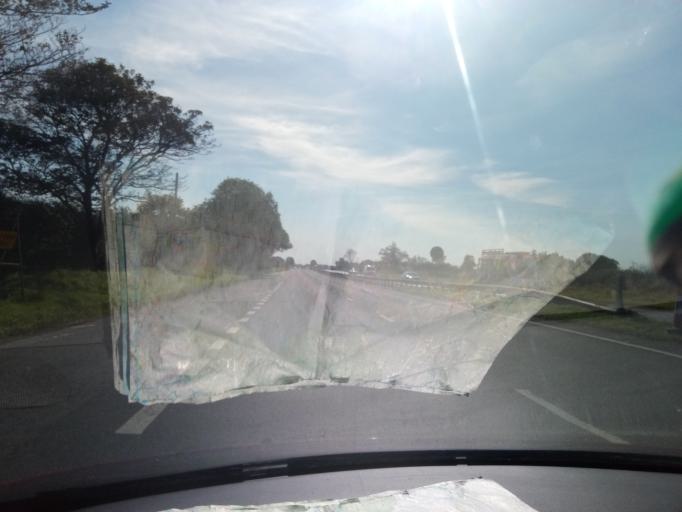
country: GB
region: England
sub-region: Stockton-on-Tees
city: Yarm
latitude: 54.4085
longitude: -1.3191
